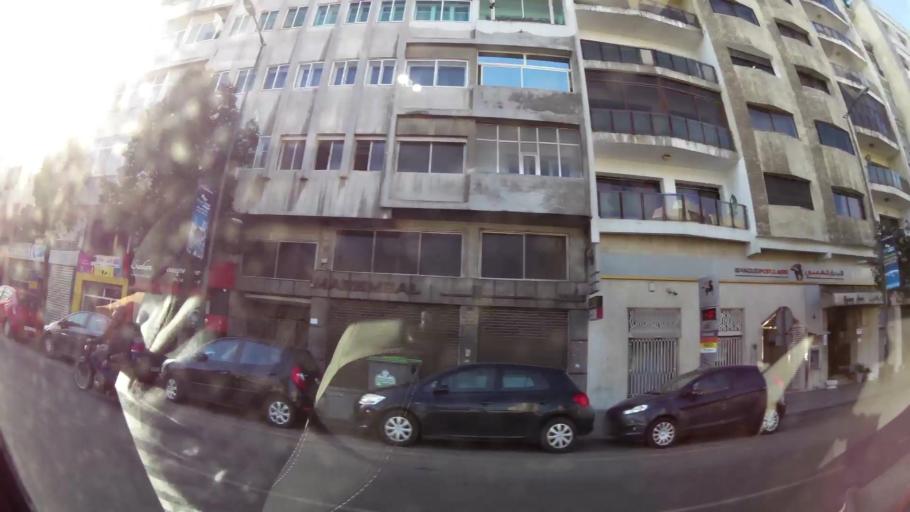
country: MA
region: Grand Casablanca
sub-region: Casablanca
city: Casablanca
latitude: 33.5981
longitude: -7.5836
